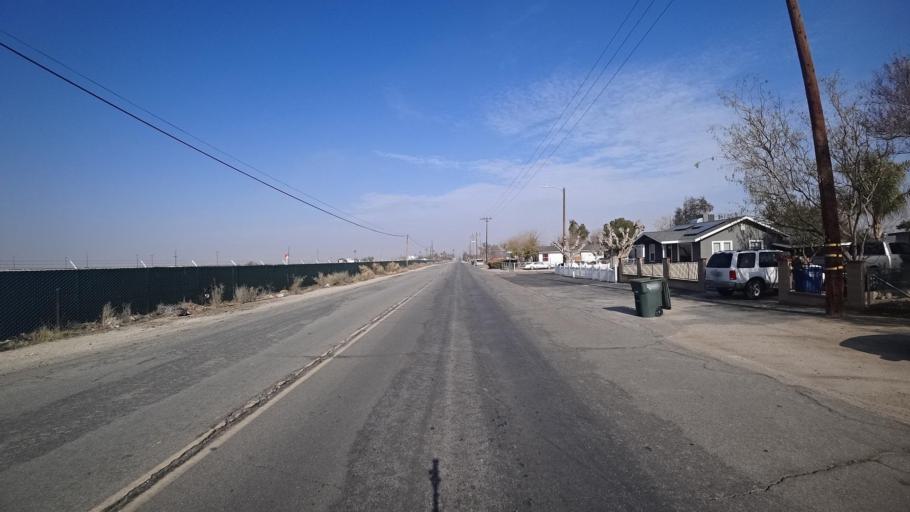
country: US
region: California
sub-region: Kern County
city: Ford City
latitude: 35.1635
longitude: -119.4652
